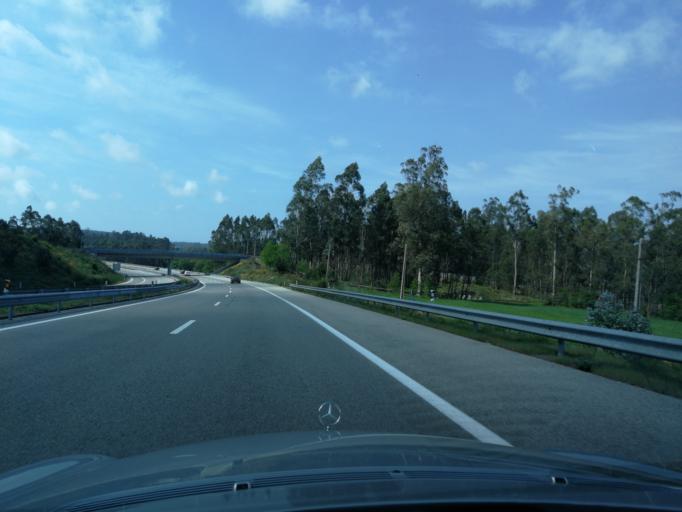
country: PT
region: Porto
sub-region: Vila do Conde
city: Arvore
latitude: 41.3899
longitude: -8.6721
